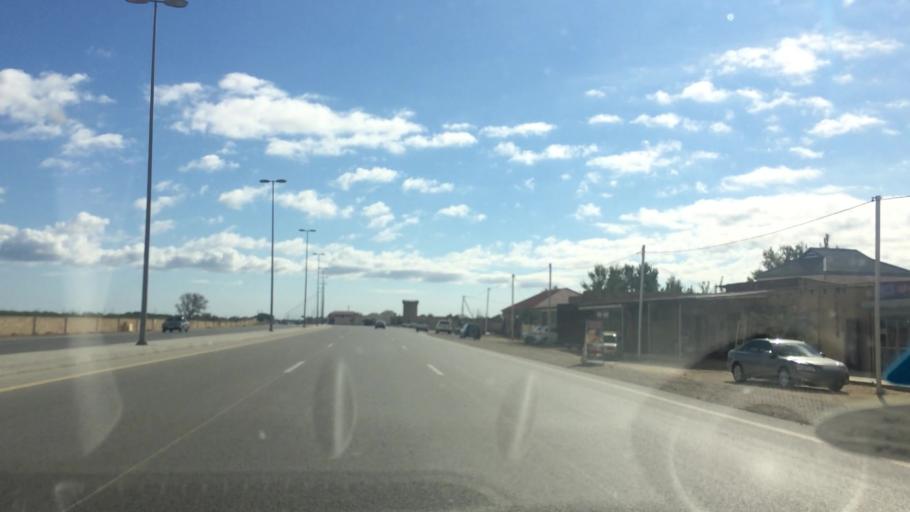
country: AZ
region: Baki
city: Qala
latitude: 40.4487
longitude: 50.1625
